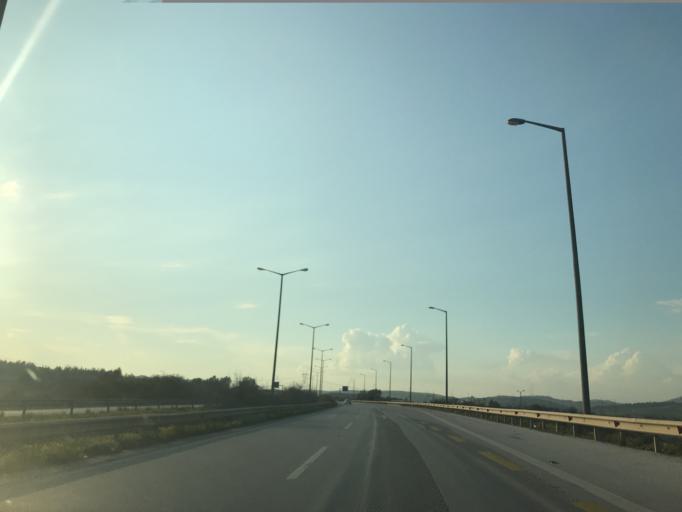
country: TR
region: Osmaniye
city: Toprakkale
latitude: 36.9742
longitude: 36.0221
